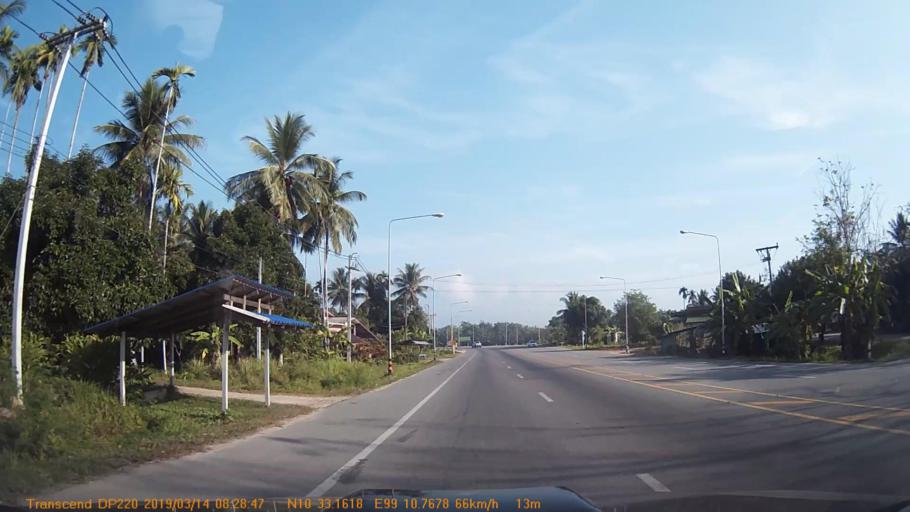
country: TH
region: Chumphon
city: Chumphon
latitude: 10.5530
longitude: 99.1794
